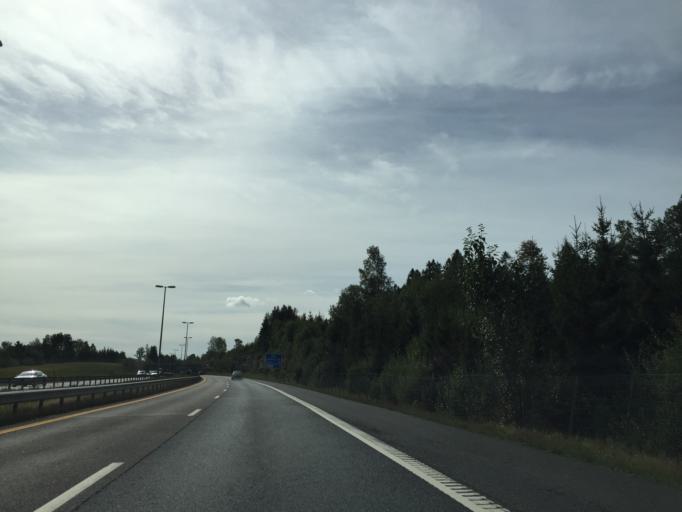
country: NO
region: Akershus
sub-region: As
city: As
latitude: 59.6852
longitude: 10.7373
